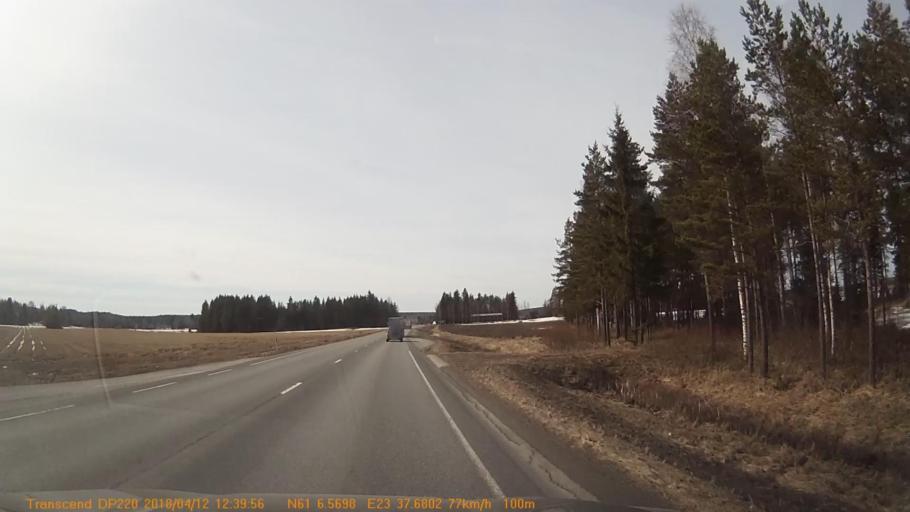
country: FI
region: Pirkanmaa
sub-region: Etelae-Pirkanmaa
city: Kylmaekoski
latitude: 61.1094
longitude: 23.6275
